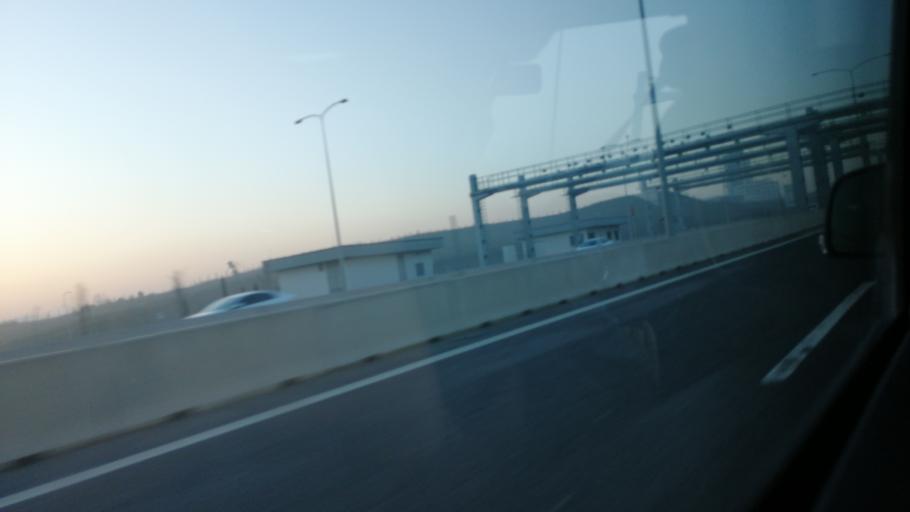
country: TR
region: Kocaeli
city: Tavsanli
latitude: 40.7846
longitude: 29.5160
